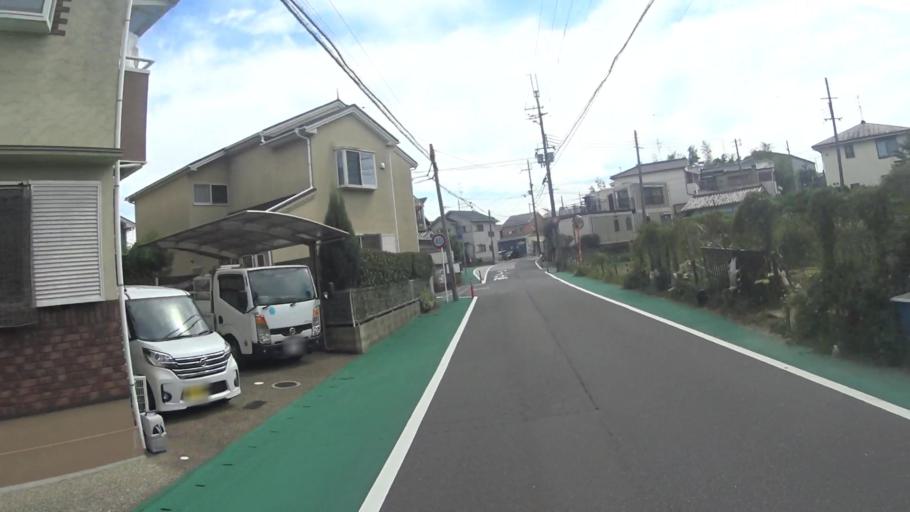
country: JP
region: Kyoto
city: Yawata
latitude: 34.8530
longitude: 135.7085
